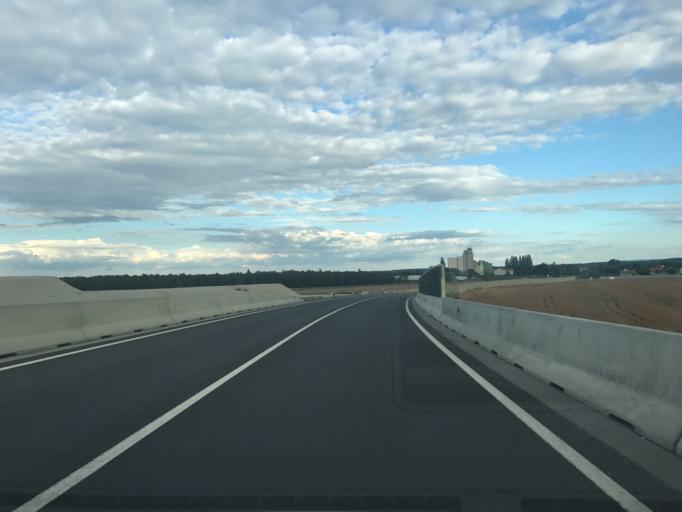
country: AT
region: Lower Austria
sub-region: Politischer Bezirk Wiener Neustadt
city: Lichtenworth
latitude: 47.8448
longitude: 16.2758
